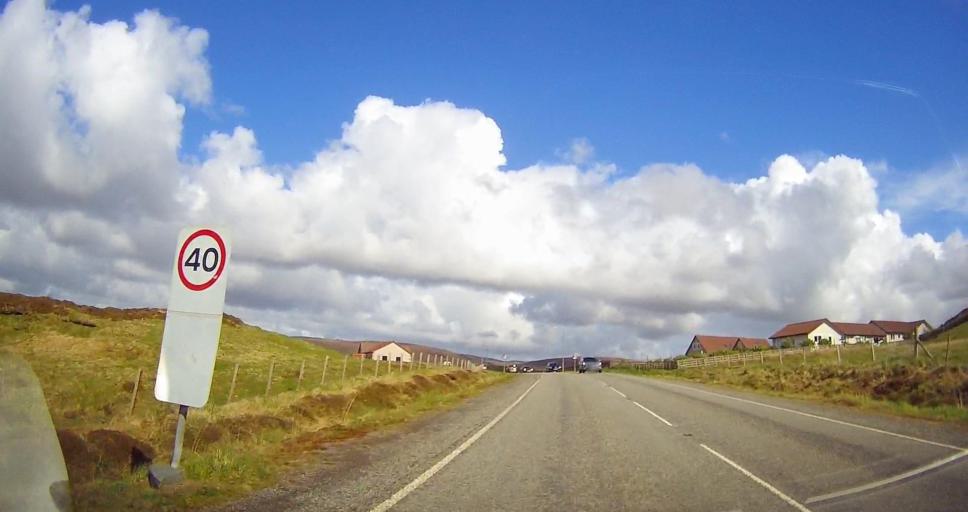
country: GB
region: Scotland
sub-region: Shetland Islands
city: Lerwick
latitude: 60.3920
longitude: -1.3736
